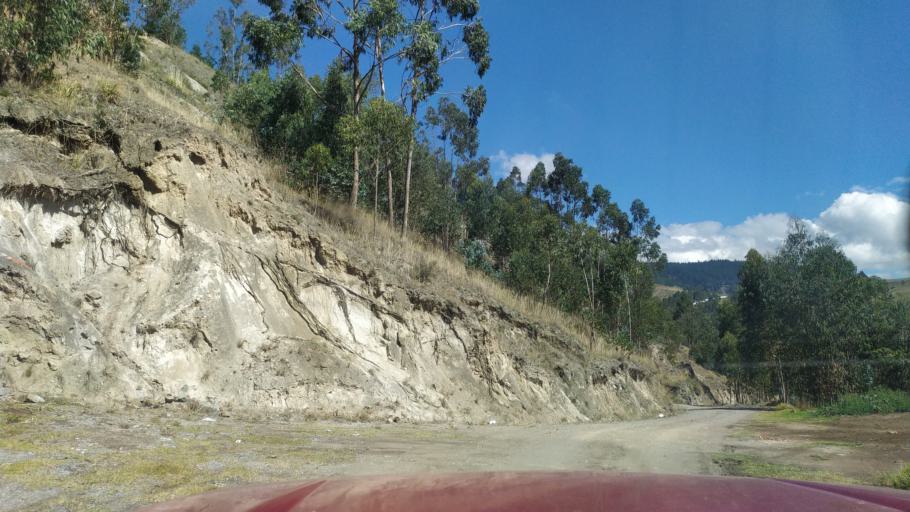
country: EC
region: Chimborazo
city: Riobamba
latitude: -1.6808
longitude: -78.6940
